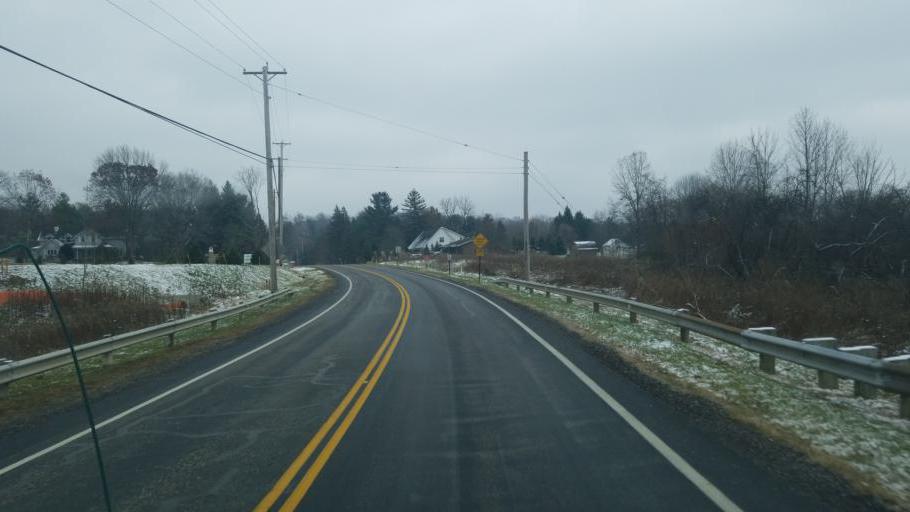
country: US
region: Ohio
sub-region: Cuyahoga County
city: Broadview Heights
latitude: 41.2771
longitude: -81.7016
